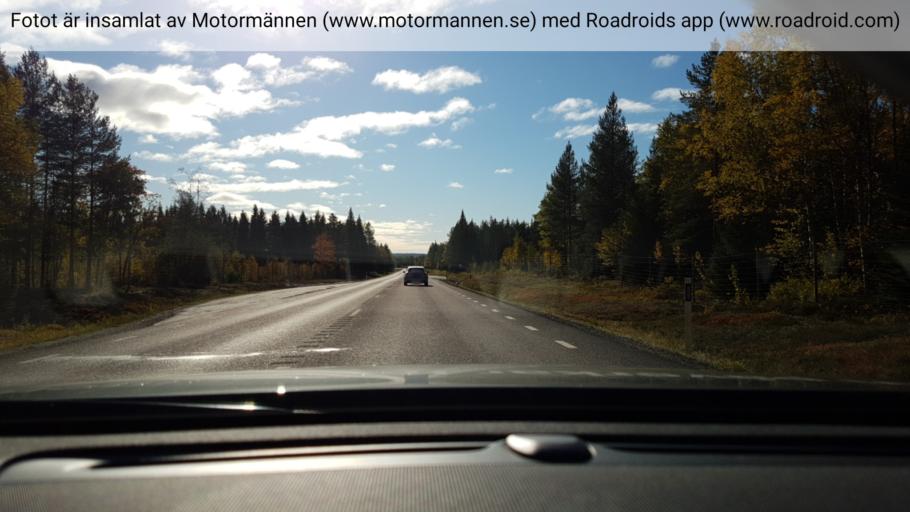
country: SE
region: Vaesterbotten
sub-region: Skelleftea Kommun
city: Burea
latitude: 64.4264
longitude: 21.2835
